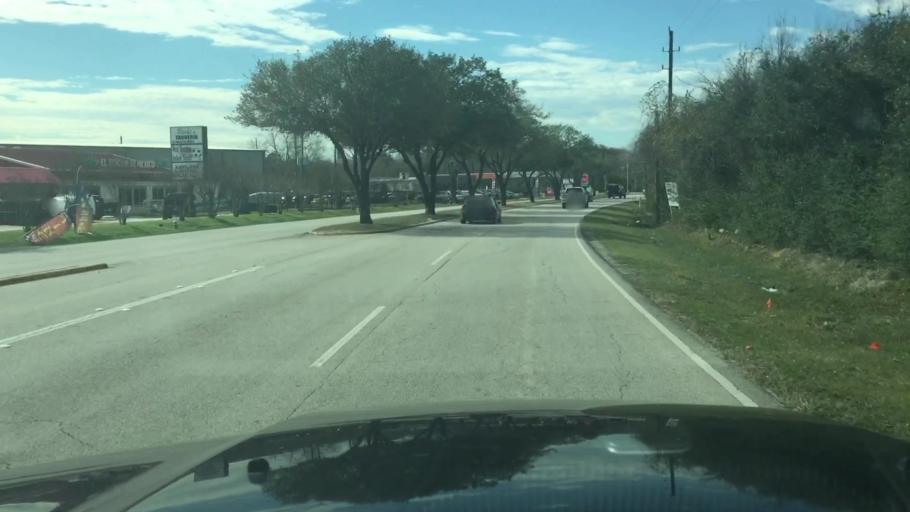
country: US
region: Texas
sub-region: Harris County
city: Oak Cliff Place
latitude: 29.8321
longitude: -95.6596
